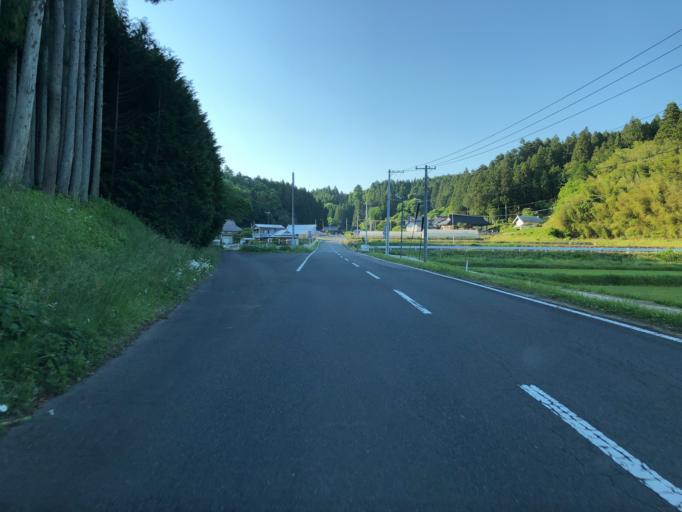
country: JP
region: Fukushima
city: Ishikawa
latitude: 36.9952
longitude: 140.4379
